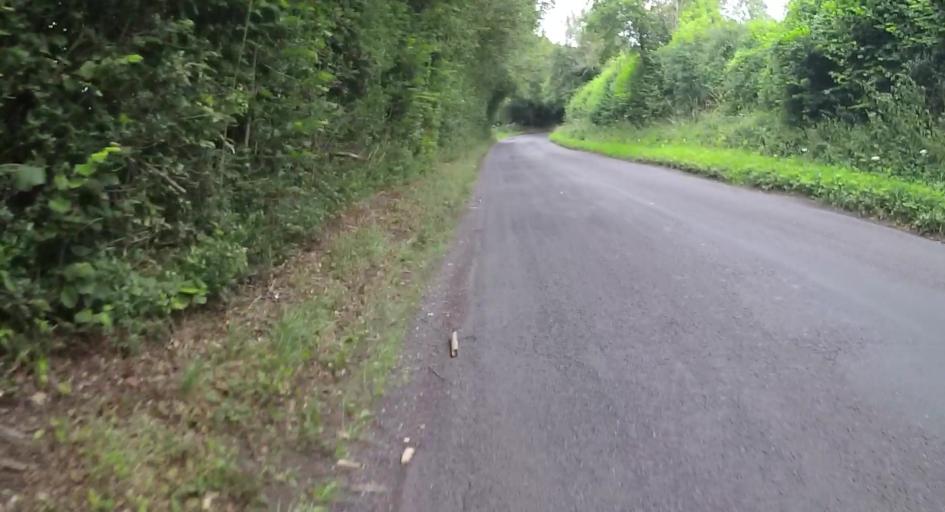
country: GB
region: England
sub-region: Hampshire
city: Bishops Waltham
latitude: 51.0240
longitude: -1.2022
